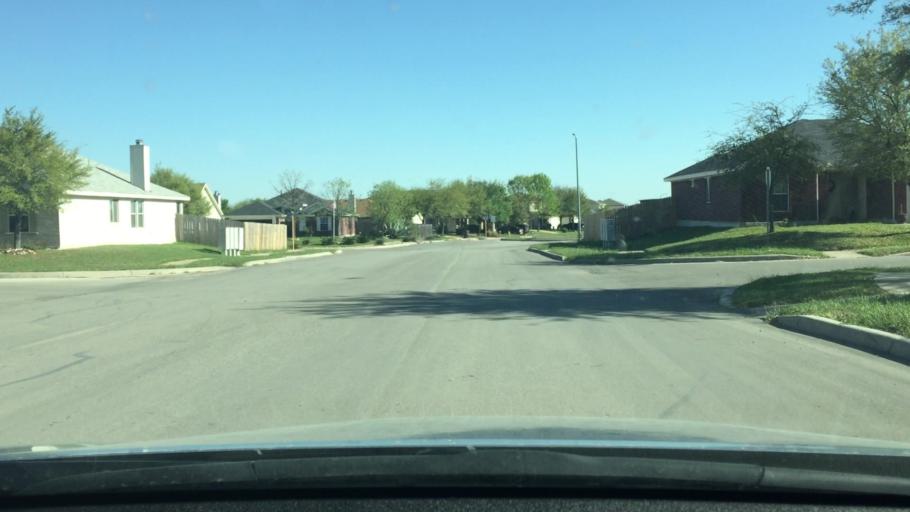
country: US
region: Texas
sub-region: Bexar County
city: Converse
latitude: 29.4689
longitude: -98.3218
